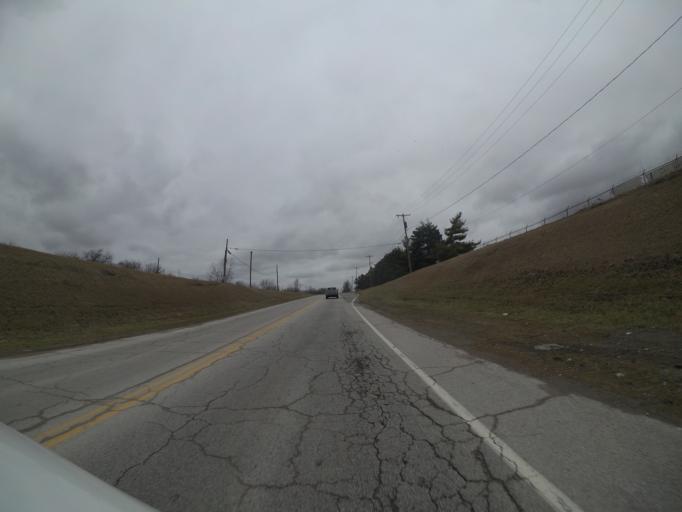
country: US
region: Ohio
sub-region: Wood County
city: Walbridge
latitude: 41.6054
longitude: -83.5123
